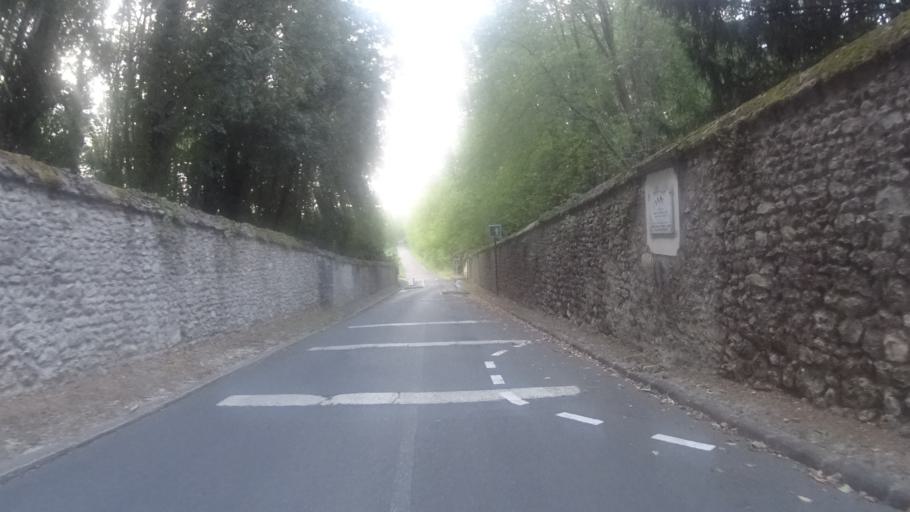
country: FR
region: Ile-de-France
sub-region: Departement de l'Essonne
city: Mennecy
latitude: 48.5700
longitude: 2.4119
